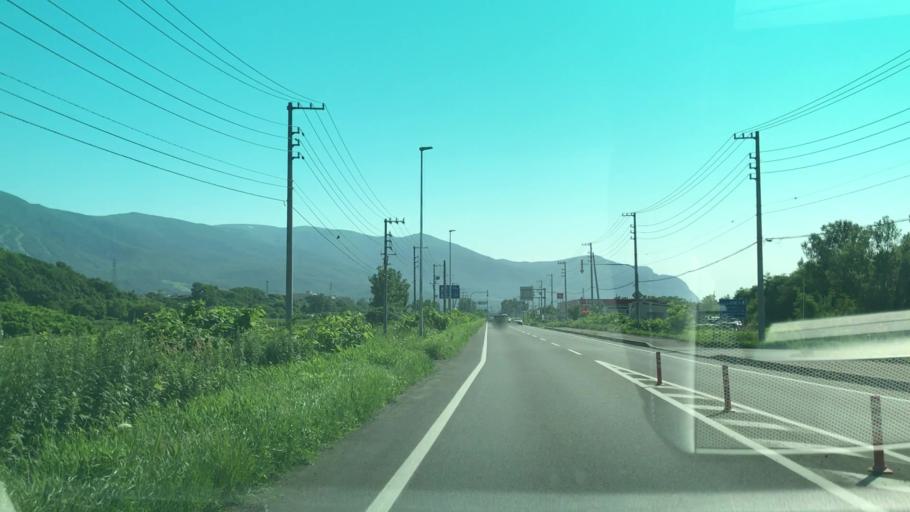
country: JP
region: Hokkaido
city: Iwanai
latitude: 42.9974
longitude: 140.5381
